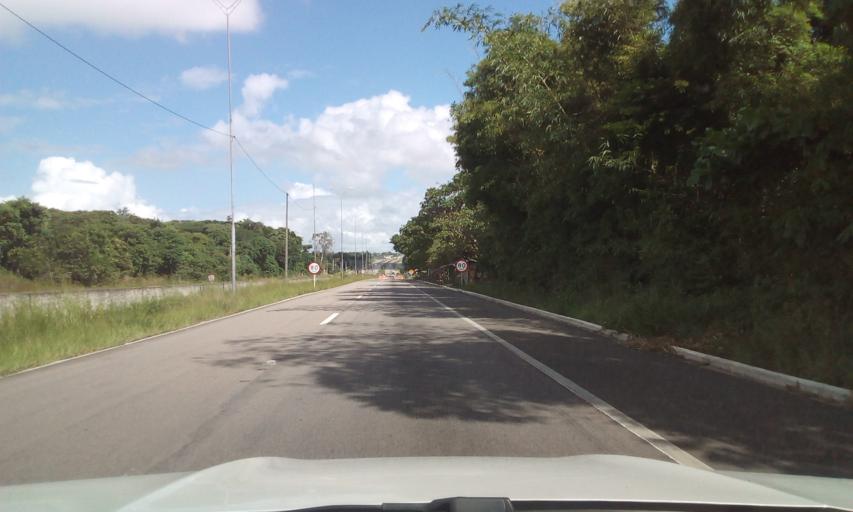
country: BR
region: Paraiba
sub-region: Conde
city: Conde
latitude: -7.3309
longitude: -34.9474
